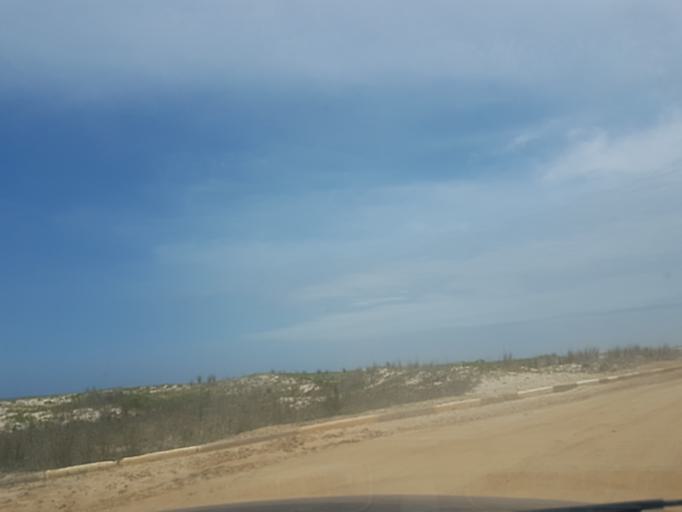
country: BR
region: Santa Catarina
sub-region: Jaguaruna
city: Jaguaruna
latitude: -28.6643
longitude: -48.9627
